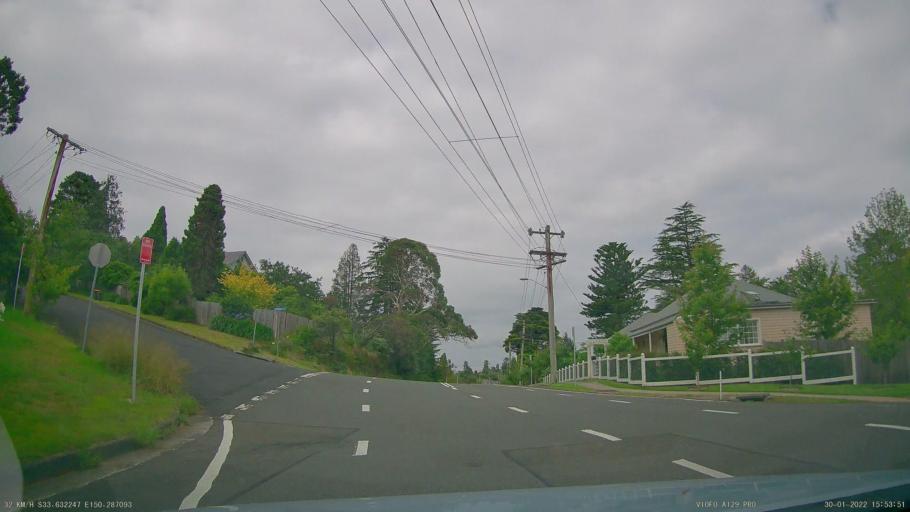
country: AU
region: New South Wales
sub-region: Blue Mountains Municipality
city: Blackheath
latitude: -33.6322
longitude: 150.2872
